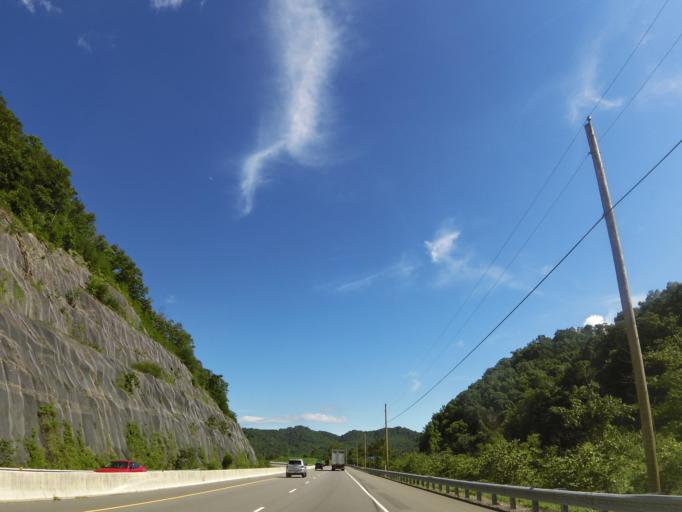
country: US
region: Tennessee
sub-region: Grainger County
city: Bean Station
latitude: 36.3501
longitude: -83.3383
